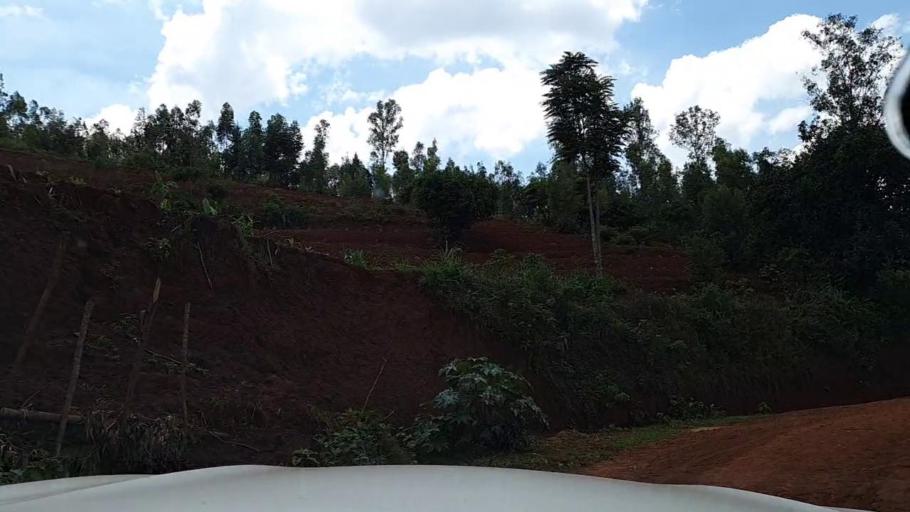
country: RW
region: Southern Province
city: Butare
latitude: -2.7444
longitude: 29.7661
